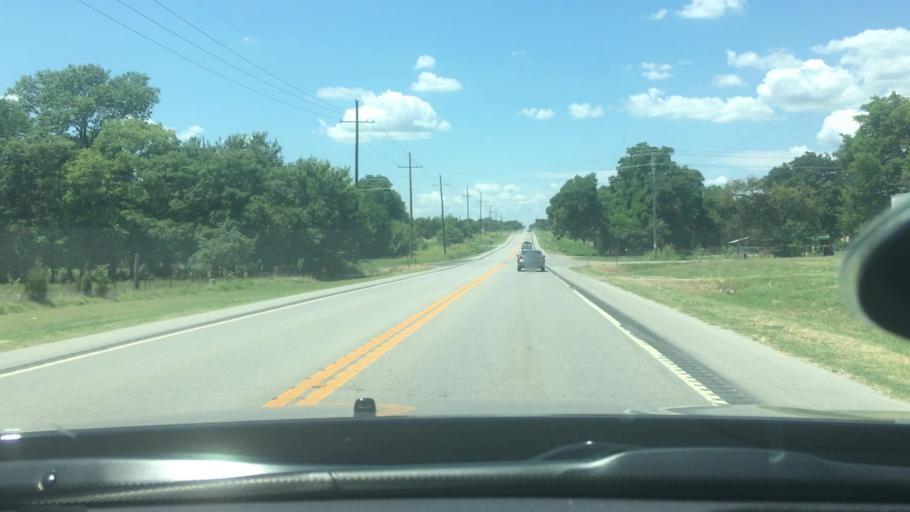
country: US
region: Oklahoma
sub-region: Bryan County
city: Durant
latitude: 33.9975
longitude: -96.3196
